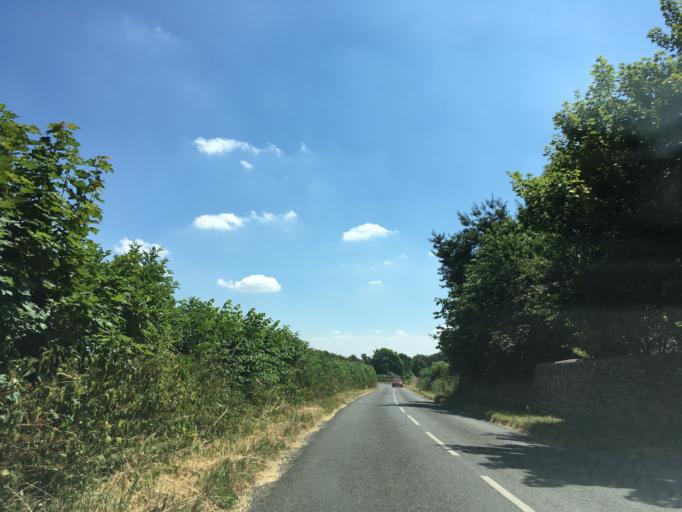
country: GB
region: England
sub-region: Gloucestershire
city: Chalford
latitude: 51.7565
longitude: -2.1454
